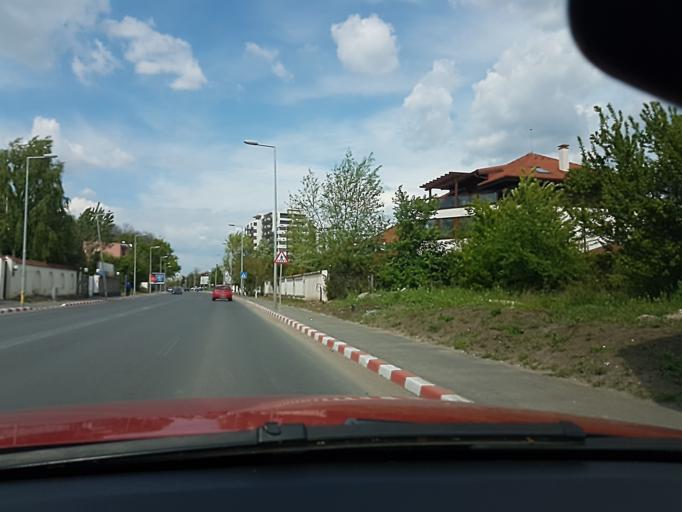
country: RO
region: Ilfov
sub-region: Comuna Tunari
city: Tunari
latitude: 44.5195
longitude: 26.1428
